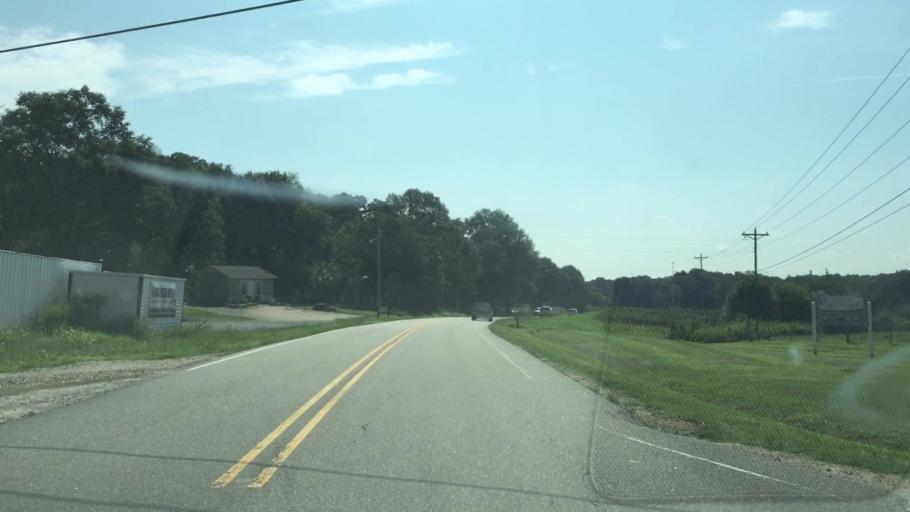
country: US
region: North Carolina
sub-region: Union County
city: Unionville
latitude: 35.1337
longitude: -80.4496
